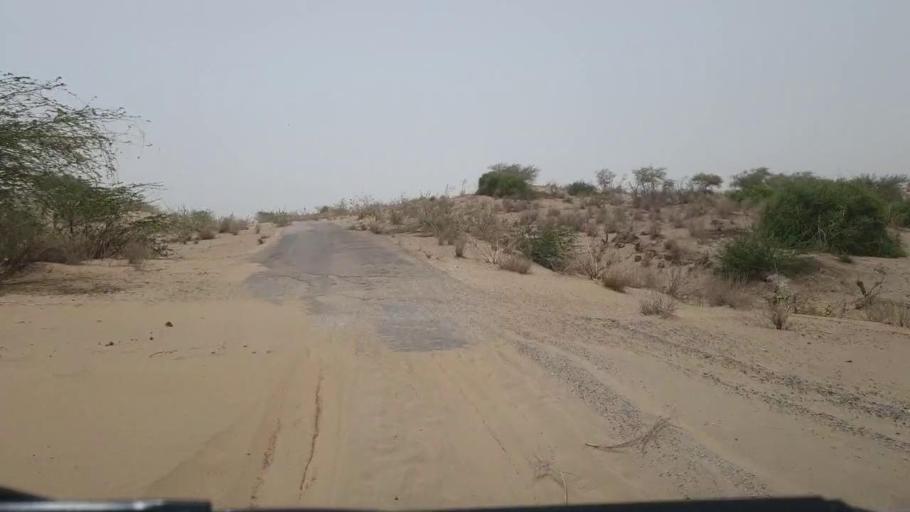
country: PK
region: Sindh
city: Naukot
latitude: 24.7787
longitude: 69.5363
